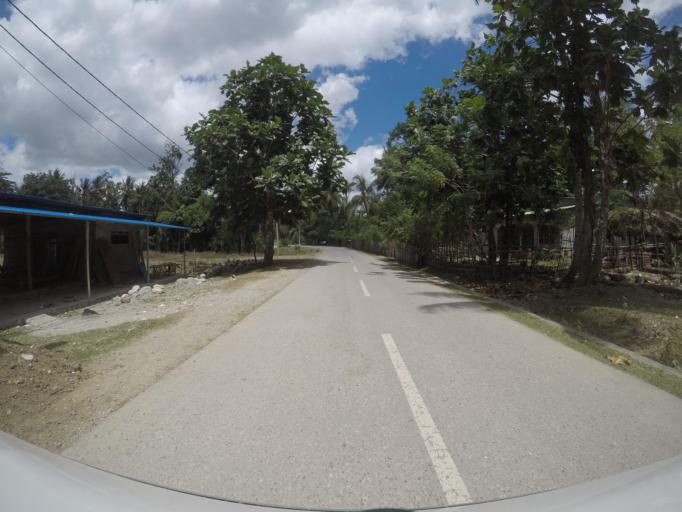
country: TL
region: Viqueque
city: Viqueque
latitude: -8.8502
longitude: 126.3651
